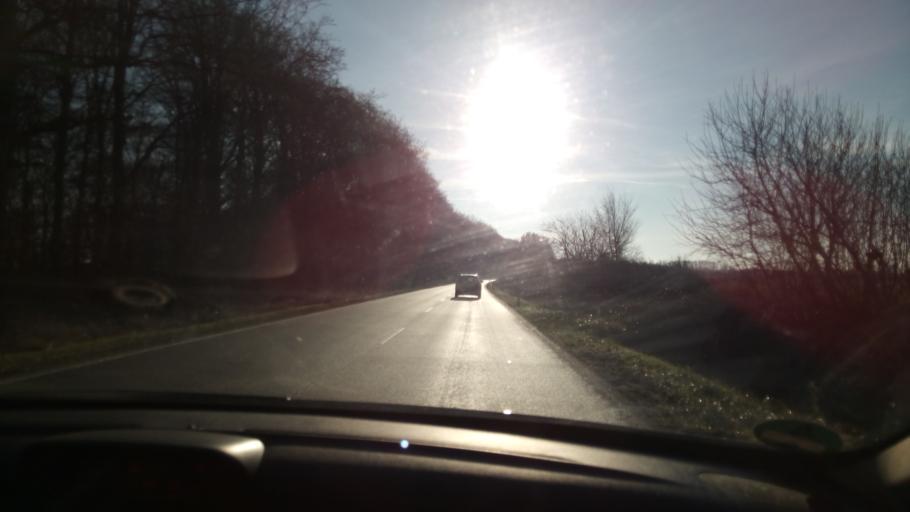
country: DE
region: Schleswig-Holstein
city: Buchhorst
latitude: 53.4016
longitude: 10.5588
